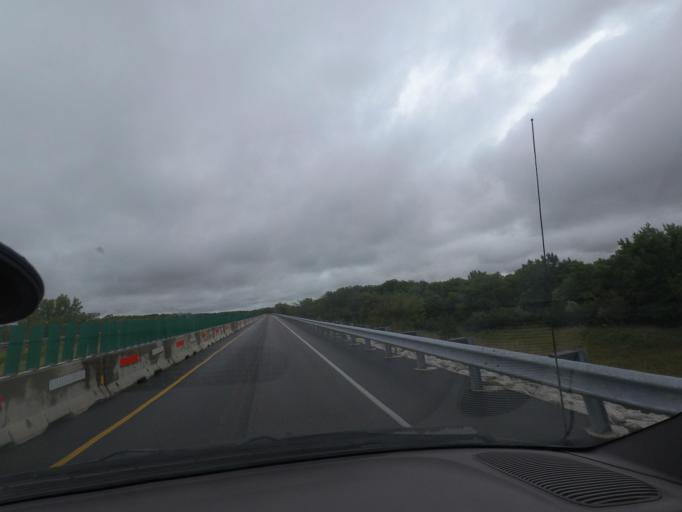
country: US
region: Illinois
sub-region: Piatt County
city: Cerro Gordo
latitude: 39.9781
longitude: -88.7976
